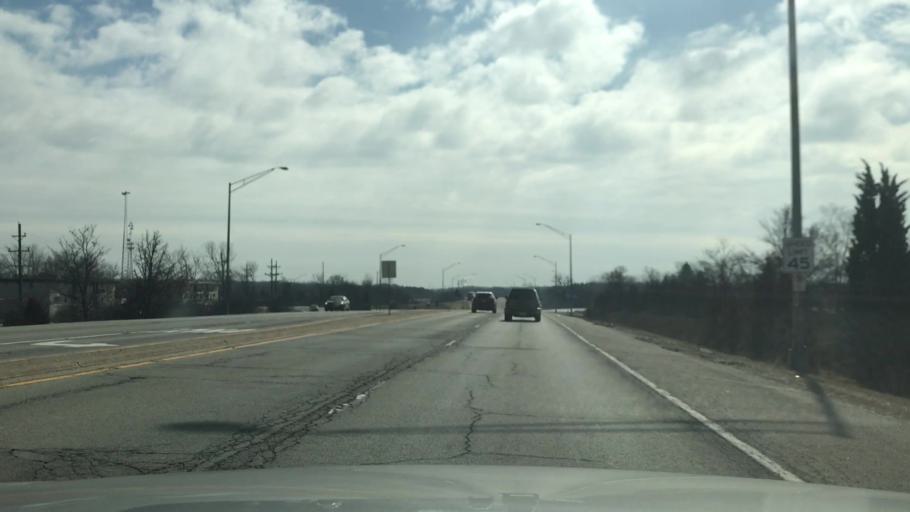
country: US
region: Illinois
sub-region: DuPage County
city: Darien
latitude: 41.7366
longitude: -87.9735
